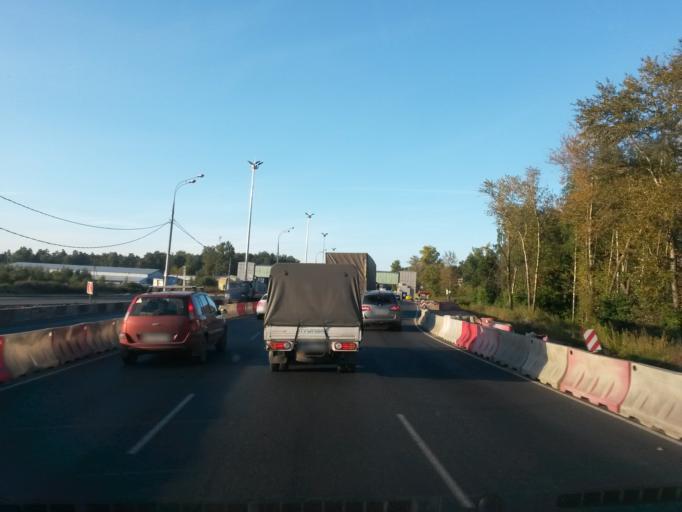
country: RU
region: Moskovskaya
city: Bolshevo
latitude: 55.9461
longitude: 37.8141
